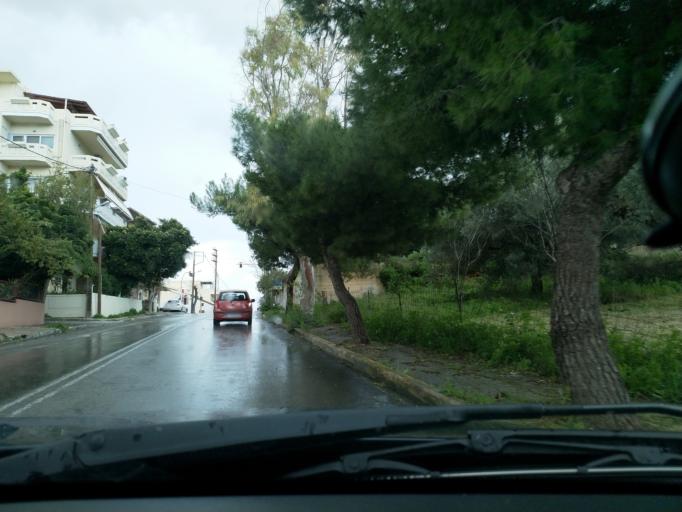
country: GR
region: Crete
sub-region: Nomos Chanias
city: Chania
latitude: 35.5138
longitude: 24.0444
